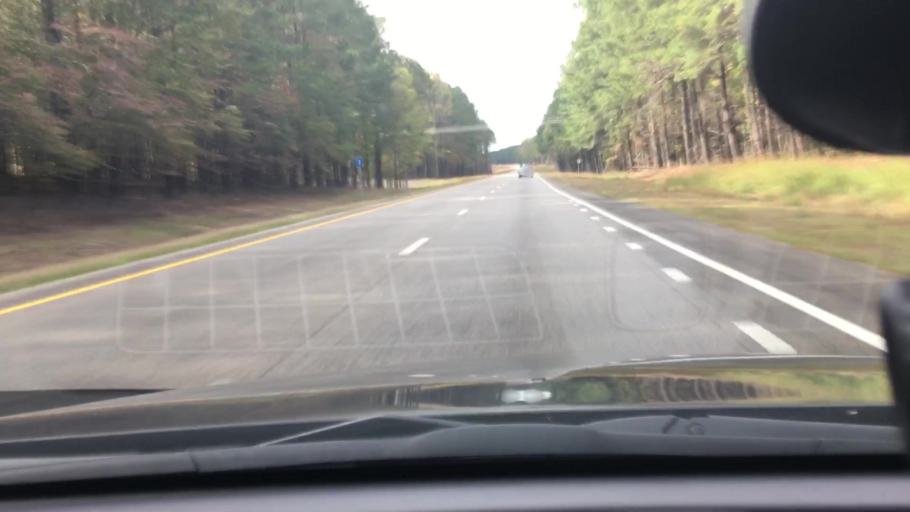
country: US
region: North Carolina
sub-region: Wake County
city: Zebulon
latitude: 35.8021
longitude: -78.1973
